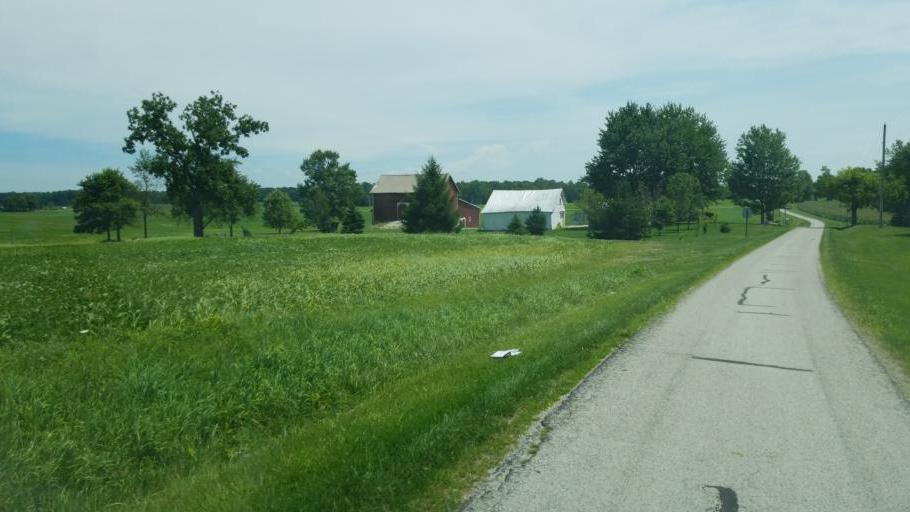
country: US
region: Ohio
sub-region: Crawford County
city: Bucyrus
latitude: 40.8742
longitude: -82.9450
